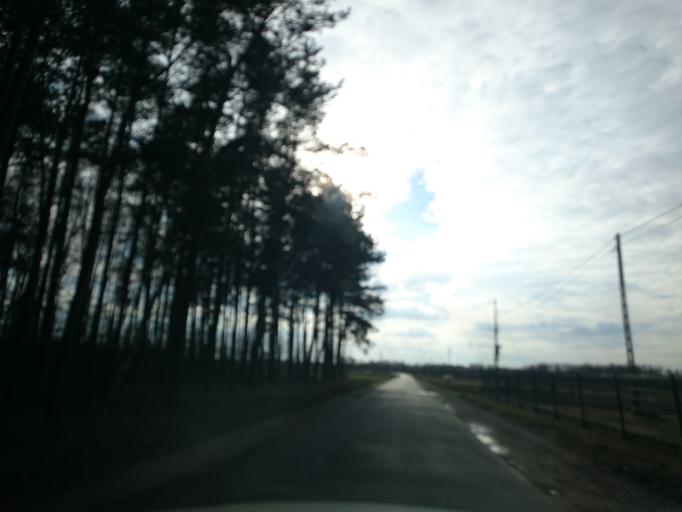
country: PL
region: Kujawsko-Pomorskie
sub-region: Powiat torunski
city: Lubicz Gorny
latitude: 53.0492
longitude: 18.8323
